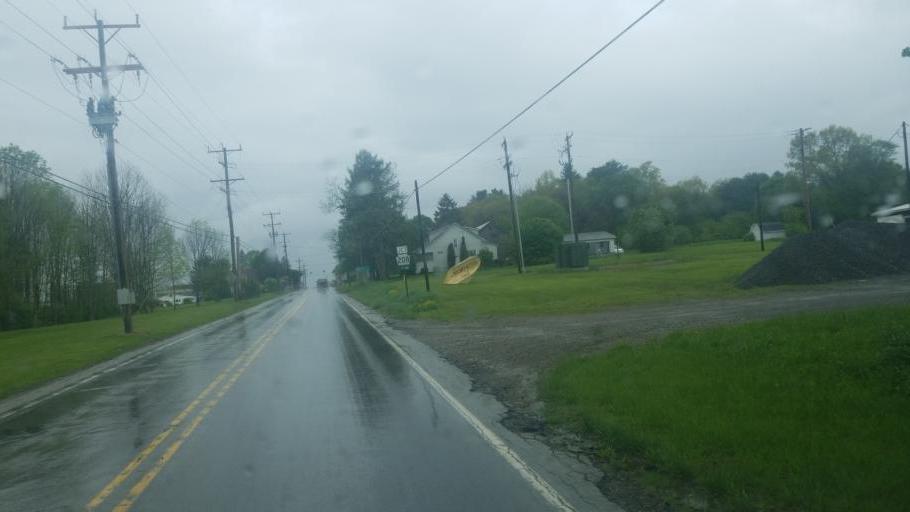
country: US
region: Pennsylvania
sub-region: Forest County
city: Tionesta
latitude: 41.3954
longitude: -79.3654
